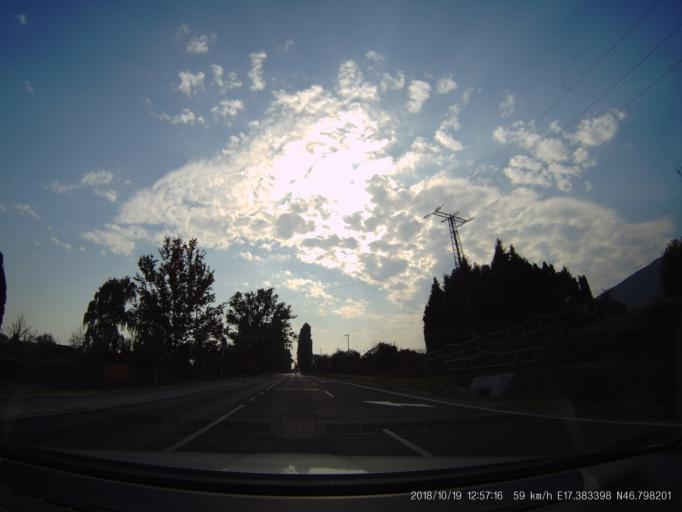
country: HU
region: Zala
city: Vonyarcvashegy
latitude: 46.7982
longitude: 17.3834
